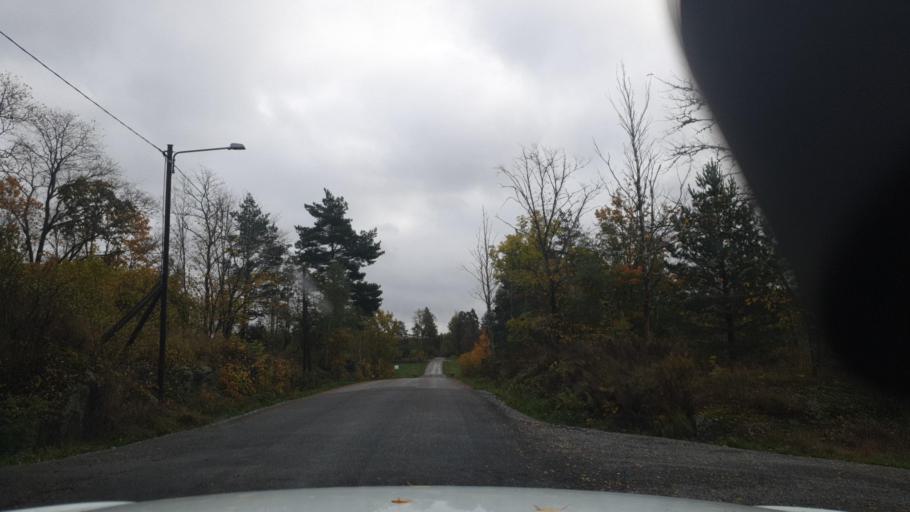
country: SE
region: Vaermland
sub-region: Karlstads Kommun
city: Valberg
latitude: 59.4198
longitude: 13.1099
